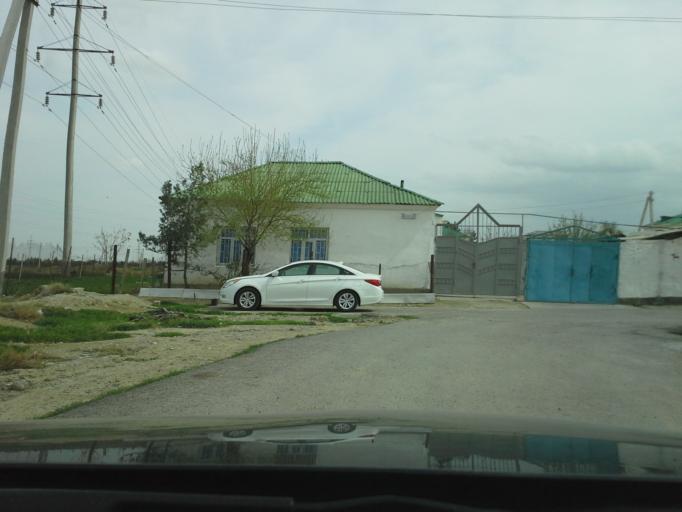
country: TM
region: Ahal
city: Abadan
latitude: 38.0636
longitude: 58.1541
